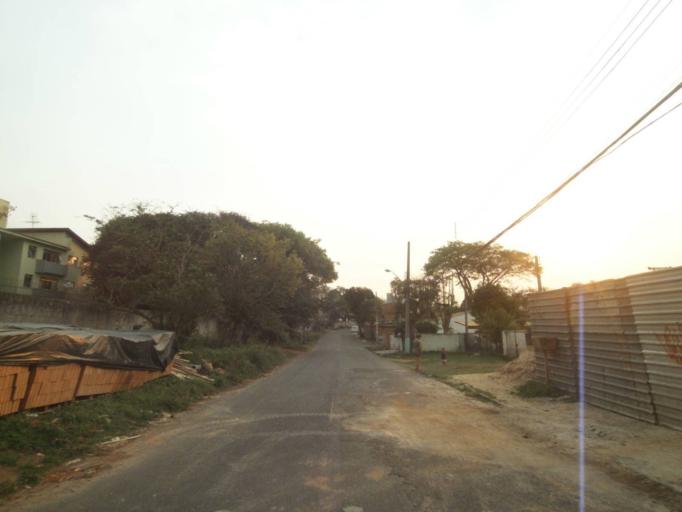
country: BR
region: Parana
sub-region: Curitiba
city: Curitiba
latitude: -25.4748
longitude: -49.2796
